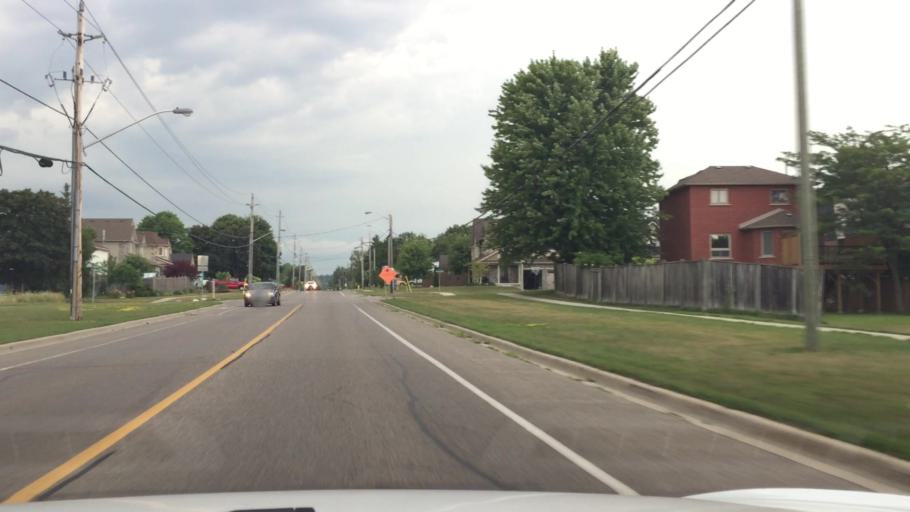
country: CA
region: Ontario
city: Oshawa
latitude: 43.9187
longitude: -78.7917
